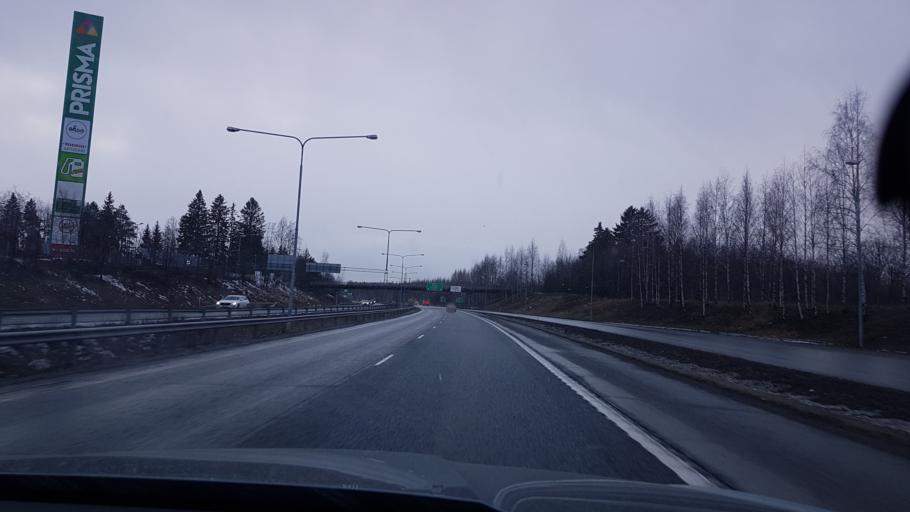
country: FI
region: Pirkanmaa
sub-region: Tampere
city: Tampere
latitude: 61.4969
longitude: 23.8811
